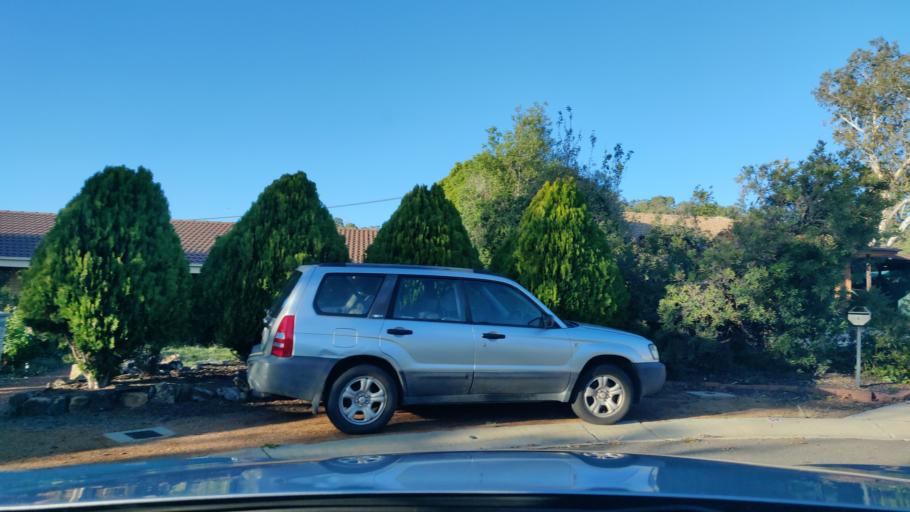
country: AU
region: Australian Capital Territory
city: Macarthur
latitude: -35.4470
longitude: 149.1263
